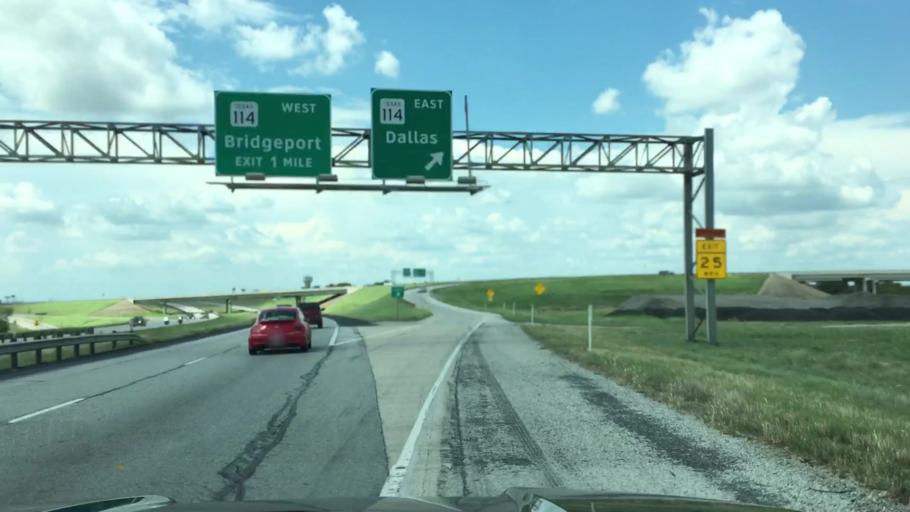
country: US
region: Texas
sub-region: Wise County
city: Rhome
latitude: 33.0434
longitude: -97.4604
